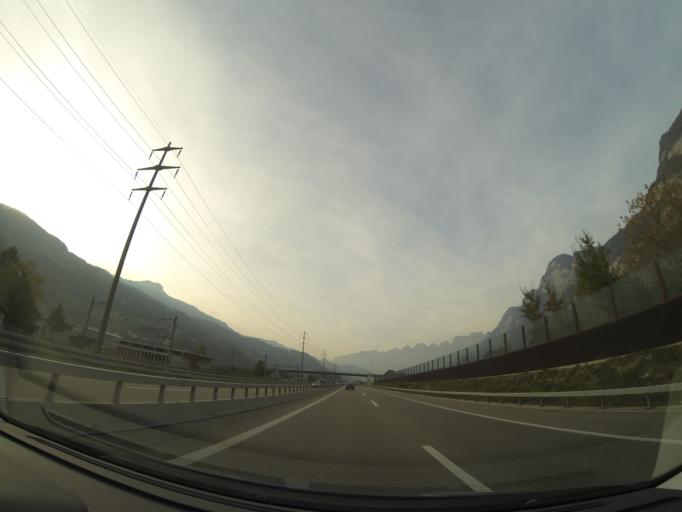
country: CH
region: Saint Gallen
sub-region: Wahlkreis Sarganserland
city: Sargans
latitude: 47.0557
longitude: 9.4080
